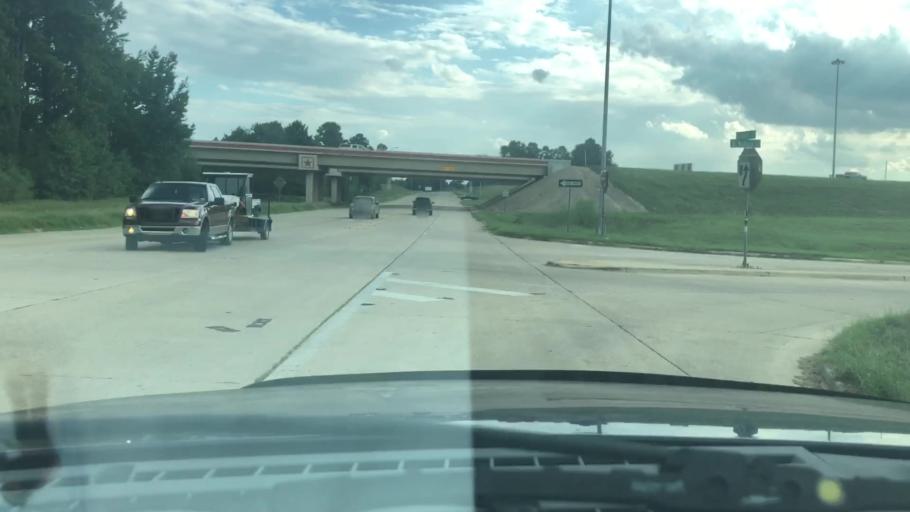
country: US
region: Texas
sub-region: Bowie County
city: Texarkana
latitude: 33.3872
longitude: -94.0663
